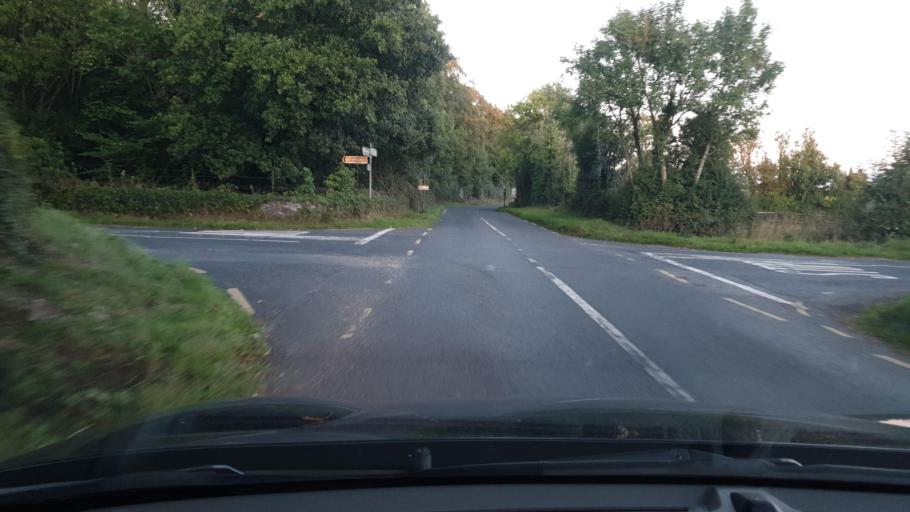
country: IE
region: Leinster
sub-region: Kildare
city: Prosperous
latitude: 53.3302
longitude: -6.7553
